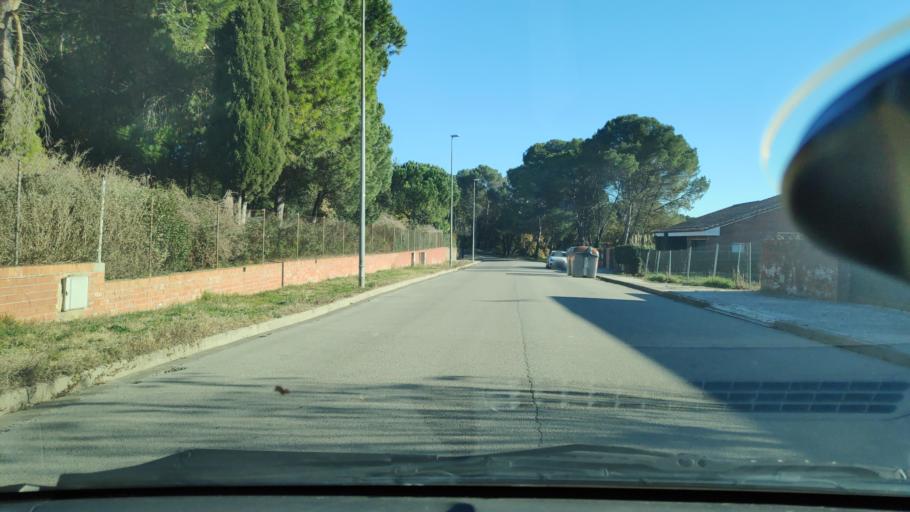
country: ES
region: Catalonia
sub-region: Provincia de Barcelona
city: Sant Quirze del Valles
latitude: 41.5368
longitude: 2.0637
